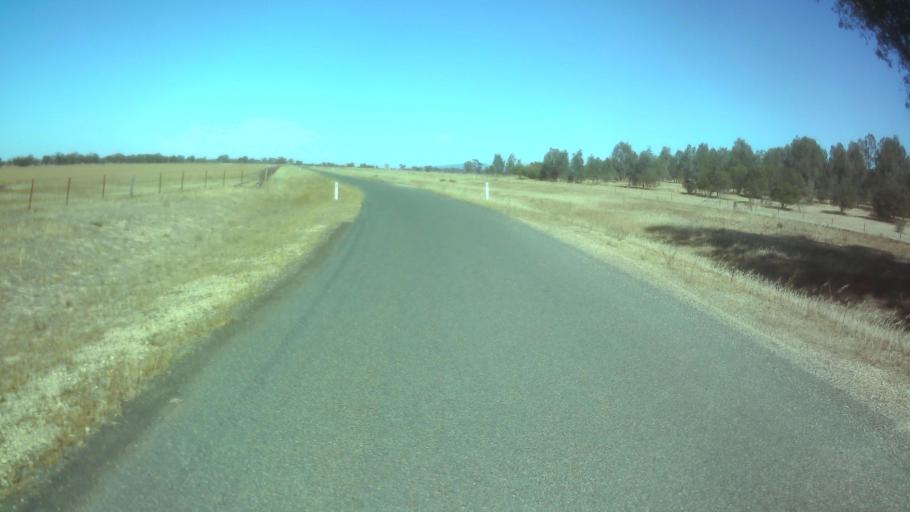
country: AU
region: New South Wales
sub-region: Weddin
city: Grenfell
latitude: -33.9957
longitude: 148.3878
